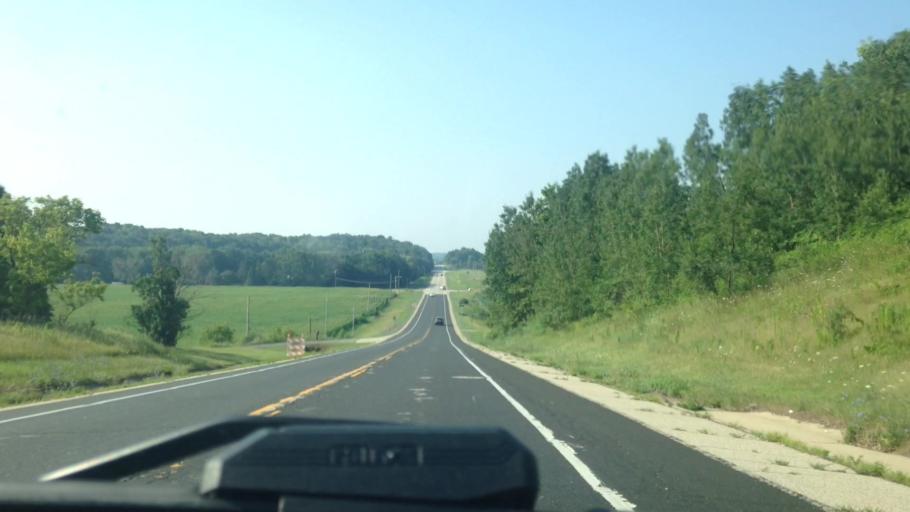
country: US
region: Wisconsin
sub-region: Waukesha County
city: Merton
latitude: 43.2122
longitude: -88.2617
